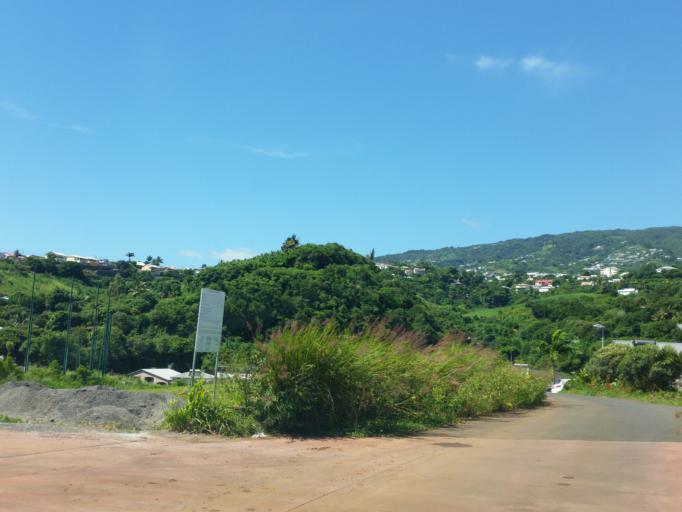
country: RE
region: Reunion
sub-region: Reunion
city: Sainte-Marie
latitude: -20.9167
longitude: 55.5207
